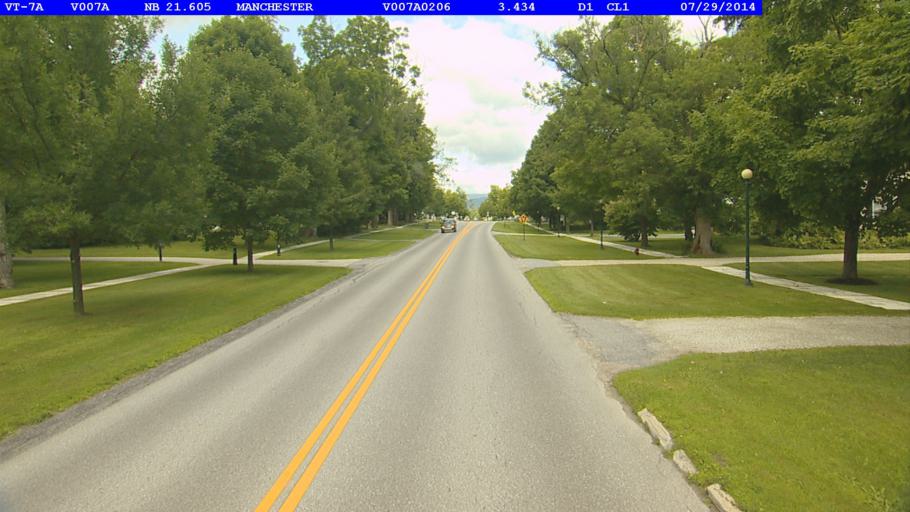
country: US
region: Vermont
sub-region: Bennington County
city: Manchester Center
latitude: 43.1601
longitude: -73.0722
